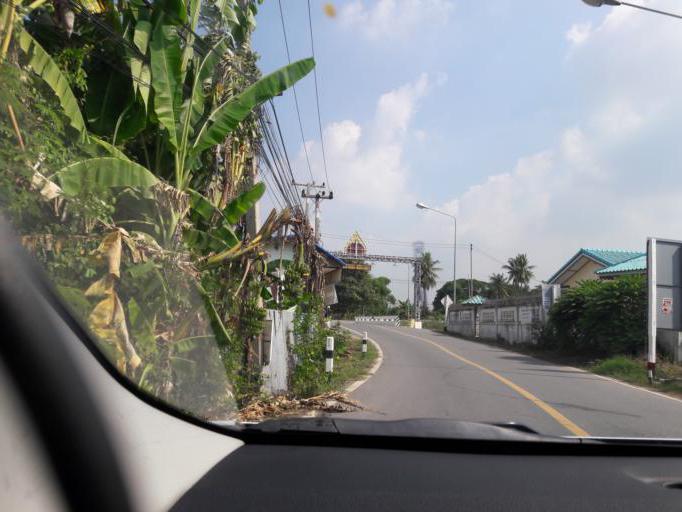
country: TH
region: Ang Thong
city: Ang Thong
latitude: 14.5617
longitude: 100.4413
